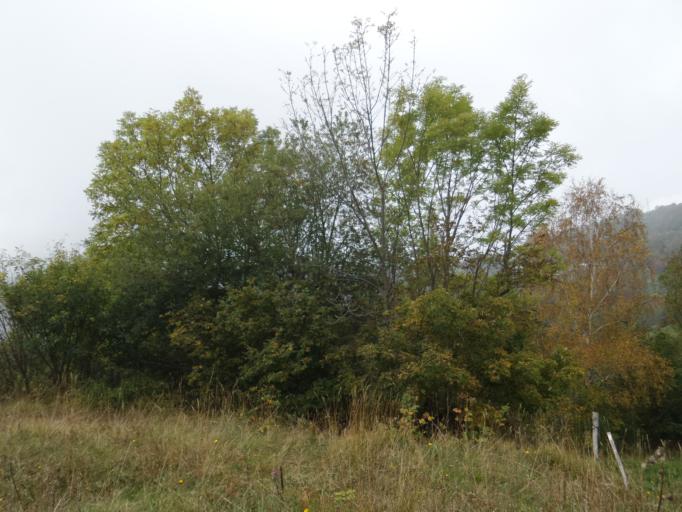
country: IT
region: Lombardy
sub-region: Provincia di Lecco
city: Ballabio
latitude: 45.9057
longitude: 9.4015
